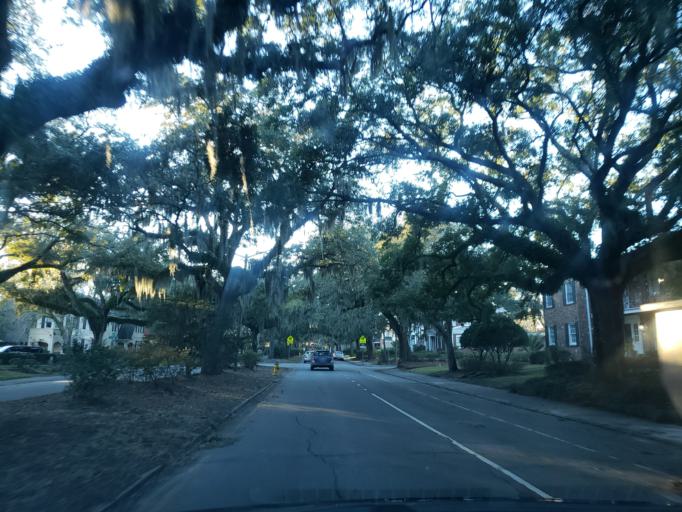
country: US
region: Georgia
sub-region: Chatham County
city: Thunderbolt
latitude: 32.0456
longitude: -81.0878
